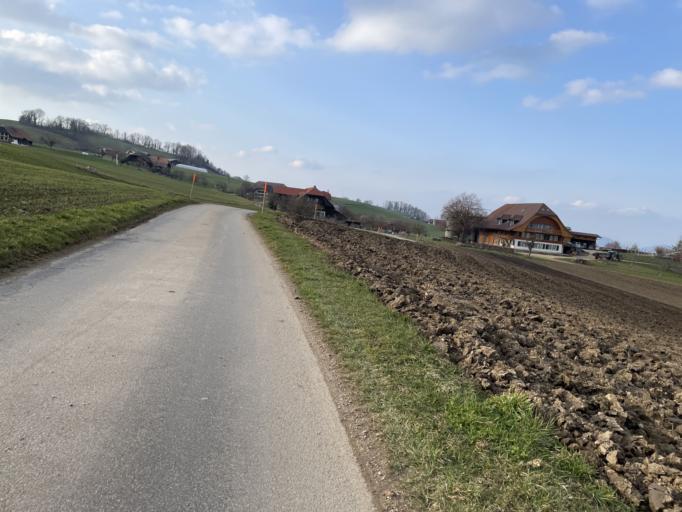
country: CH
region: Bern
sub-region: Bern-Mittelland District
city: Rubigen
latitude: 46.8700
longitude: 7.5274
